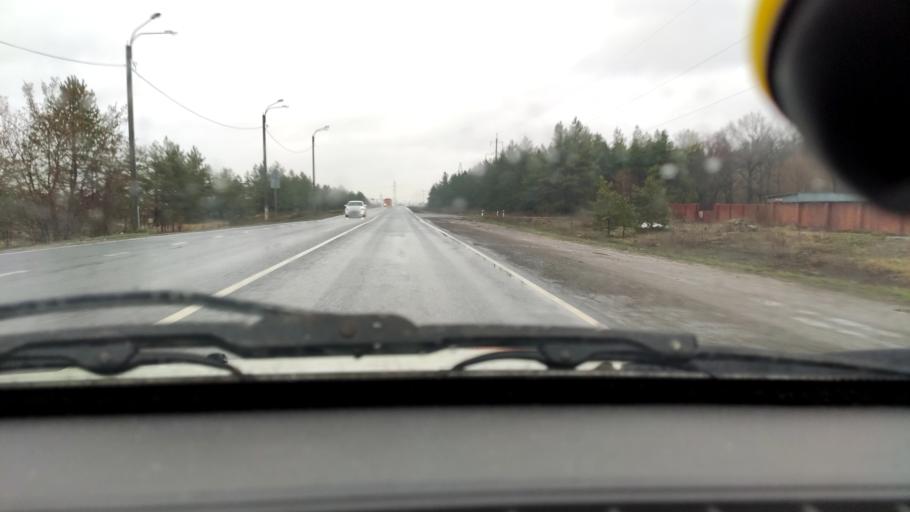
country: RU
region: Samara
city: Zhigulevsk
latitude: 53.5677
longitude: 49.5486
